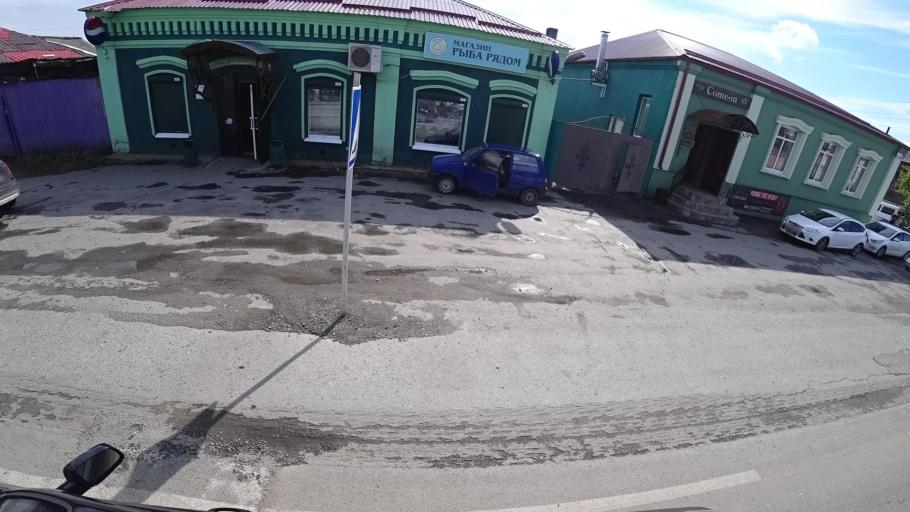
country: RU
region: Sverdlovsk
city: Kamyshlov
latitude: 56.8411
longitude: 62.7098
